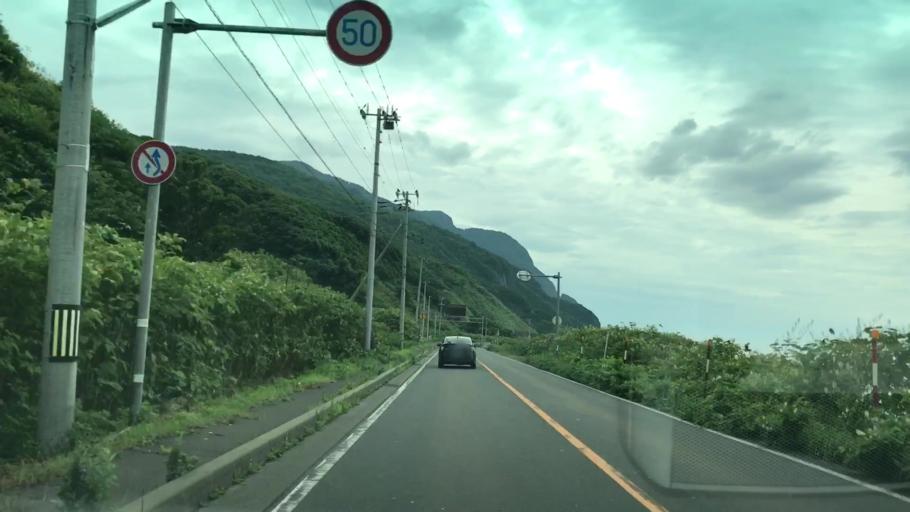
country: JP
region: Hokkaido
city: Iwanai
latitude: 42.9641
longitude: 140.4675
